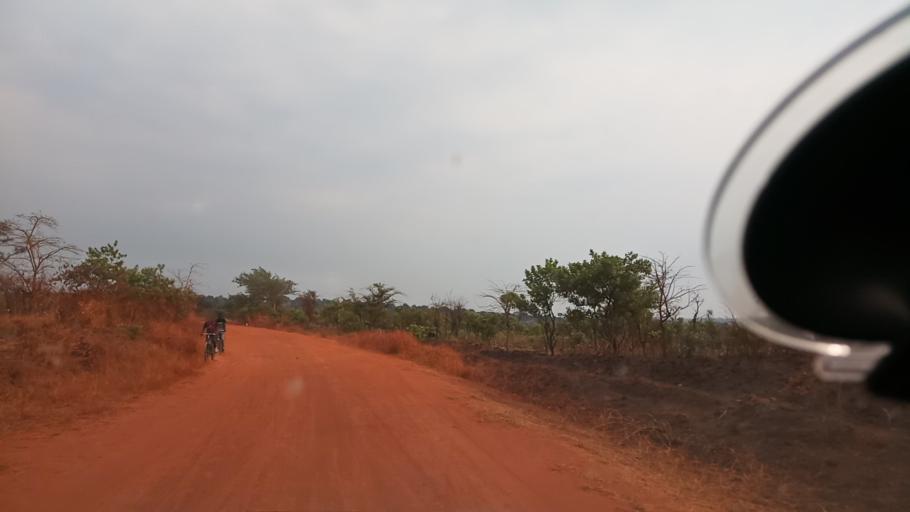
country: ZM
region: Luapula
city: Nchelenge
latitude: -9.1103
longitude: 28.3032
